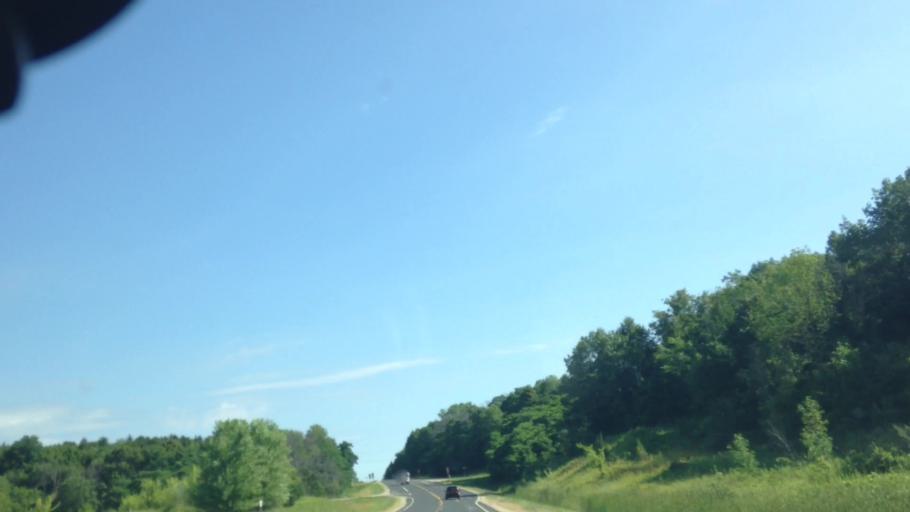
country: US
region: Wisconsin
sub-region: Washington County
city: Slinger
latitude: 43.3673
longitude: -88.2592
